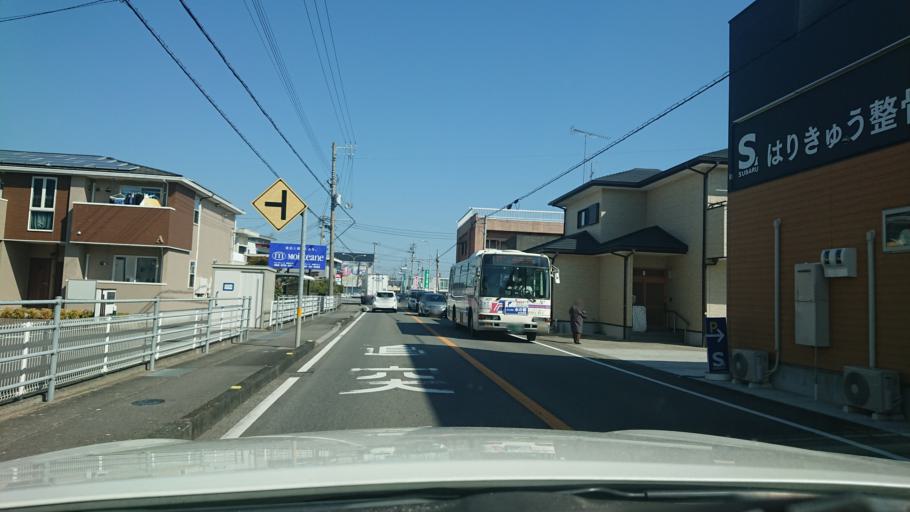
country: JP
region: Tokushima
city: Anan
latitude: 33.9494
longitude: 134.6270
